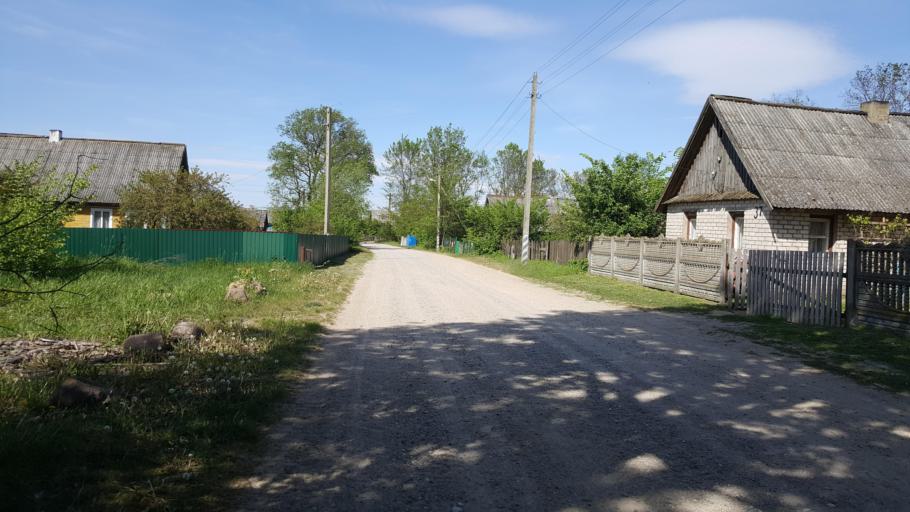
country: BY
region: Brest
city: Zhabinka
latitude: 52.3164
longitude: 24.0414
